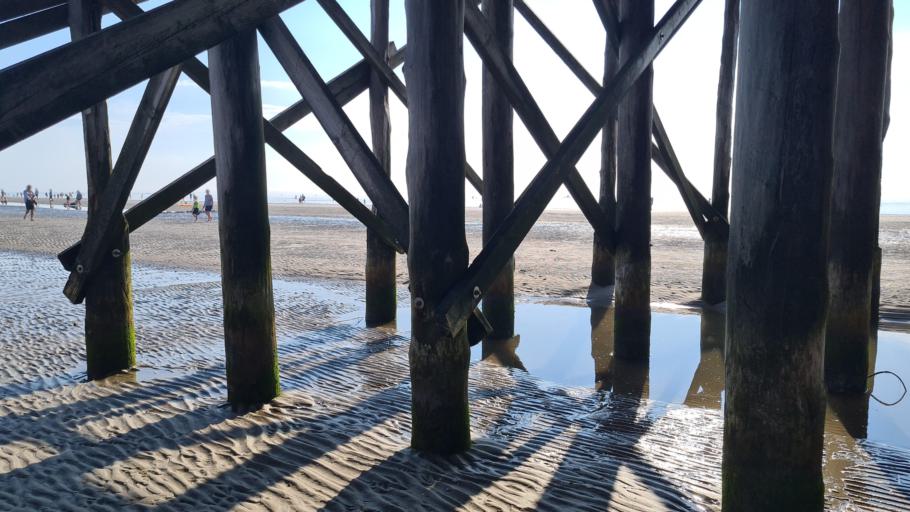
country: DE
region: Schleswig-Holstein
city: Sankt Peter-Ording
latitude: 54.3354
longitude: 8.5913
